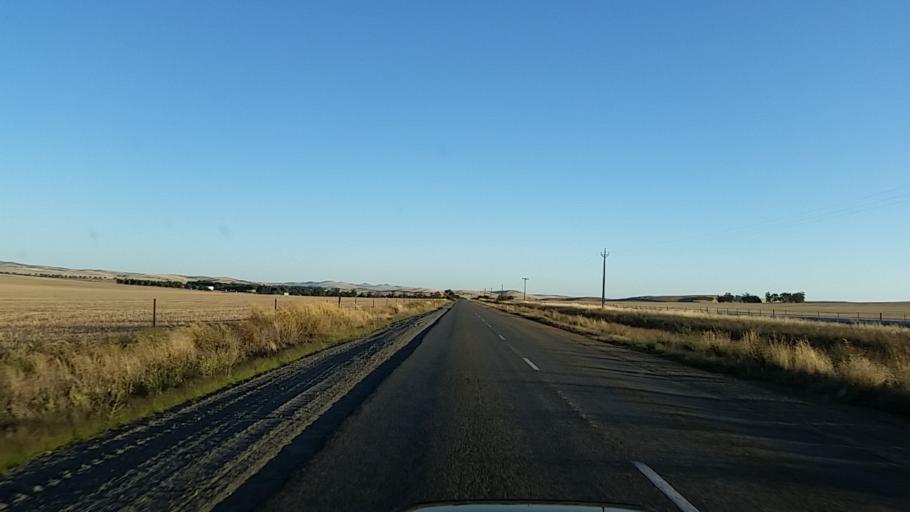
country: AU
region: South Australia
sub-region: Northern Areas
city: Jamestown
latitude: -33.4797
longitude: 138.5970
